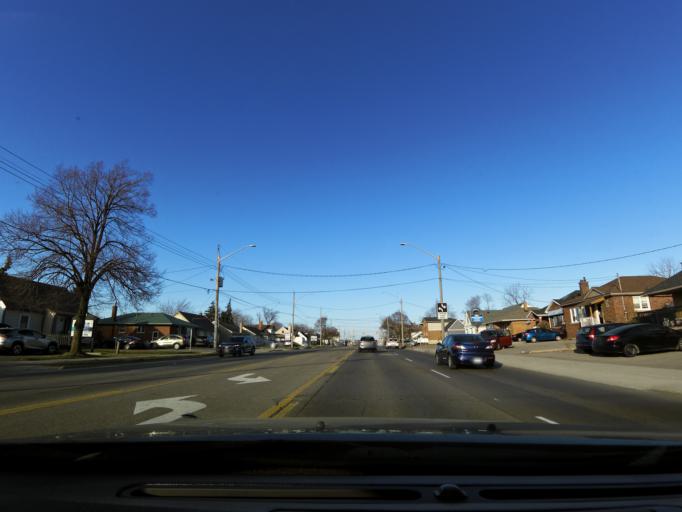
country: CA
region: Ontario
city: Hamilton
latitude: 43.2318
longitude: -79.8803
